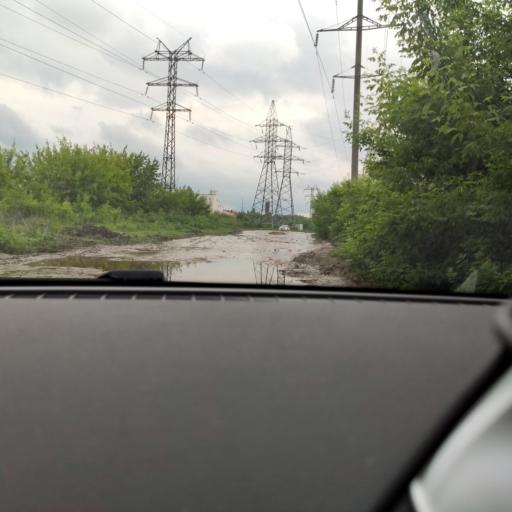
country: RU
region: Samara
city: Petra-Dubrava
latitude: 53.2643
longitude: 50.2999
